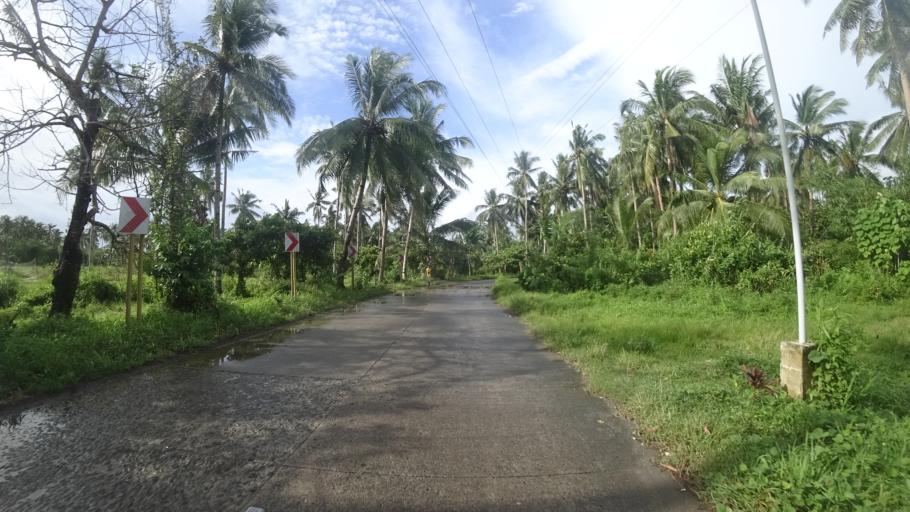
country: PH
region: Eastern Visayas
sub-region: Province of Leyte
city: MacArthur
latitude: 10.8233
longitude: 124.9930
